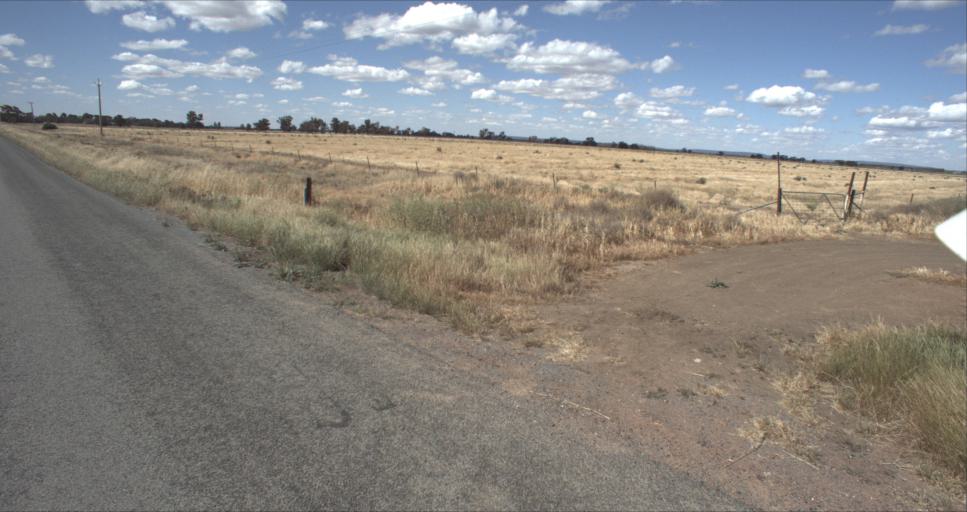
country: AU
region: New South Wales
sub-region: Leeton
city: Leeton
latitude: -34.4978
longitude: 146.2460
